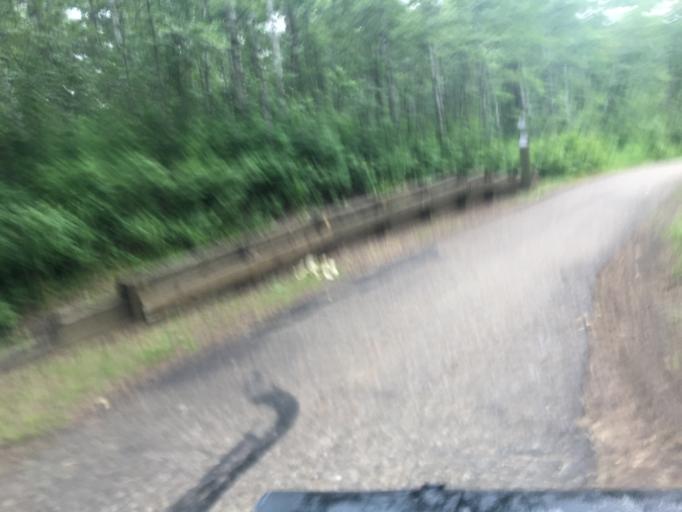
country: CA
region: Alberta
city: Grande Prairie
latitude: 55.1483
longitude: -118.8010
